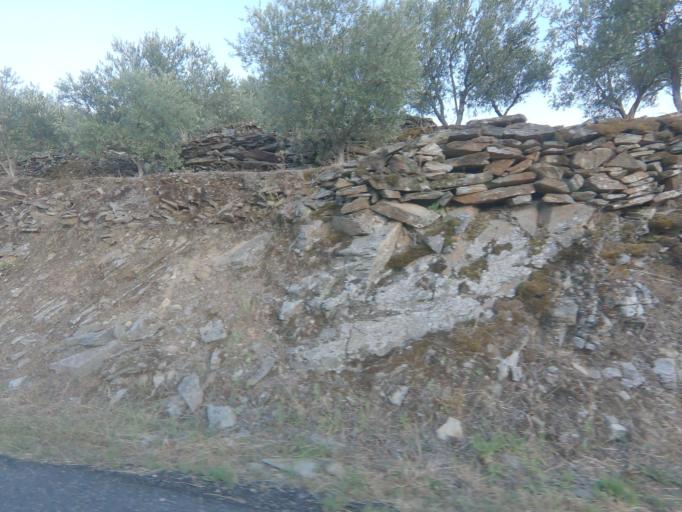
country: PT
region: Viseu
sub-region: Armamar
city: Armamar
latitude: 41.1690
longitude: -7.6856
